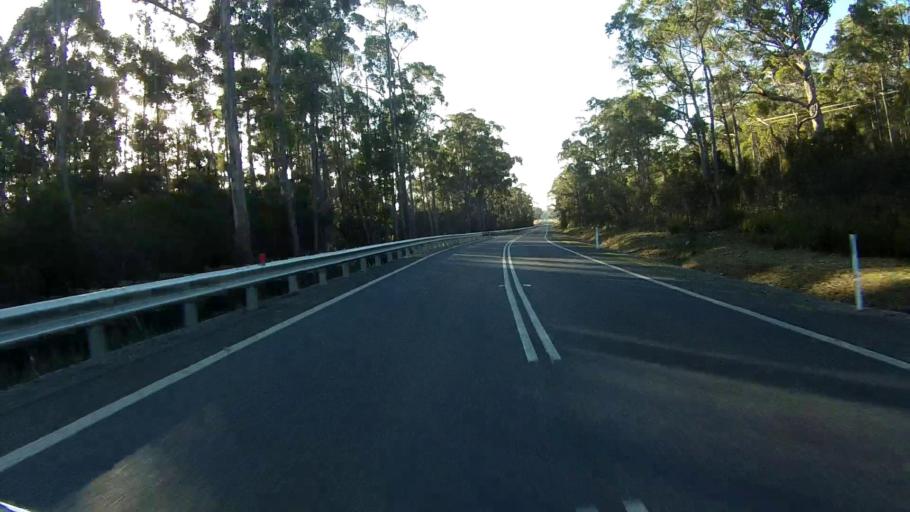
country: AU
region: Tasmania
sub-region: Clarence
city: Sandford
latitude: -43.0775
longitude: 147.8624
